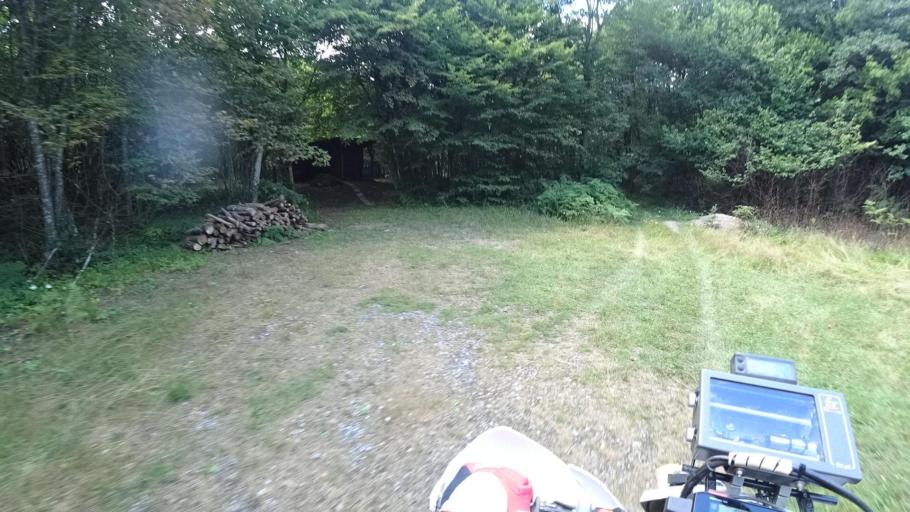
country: HR
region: Karlovacka
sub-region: Grad Ogulin
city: Ogulin
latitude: 45.2550
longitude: 15.1891
